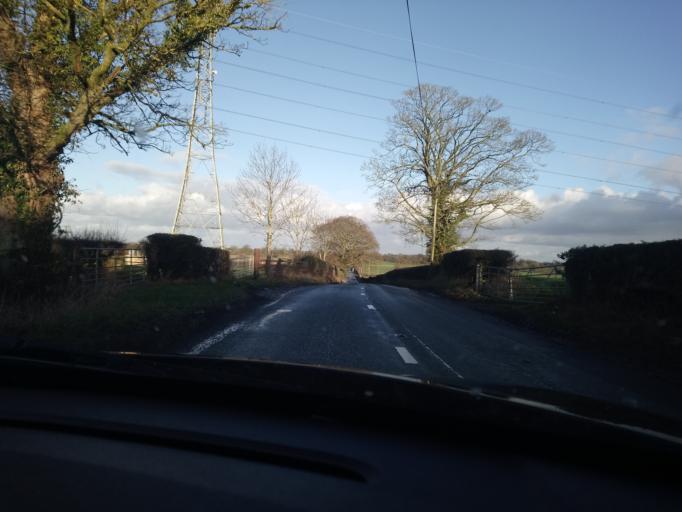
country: GB
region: Wales
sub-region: Wrexham
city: Overton
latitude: 52.9240
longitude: -2.9710
